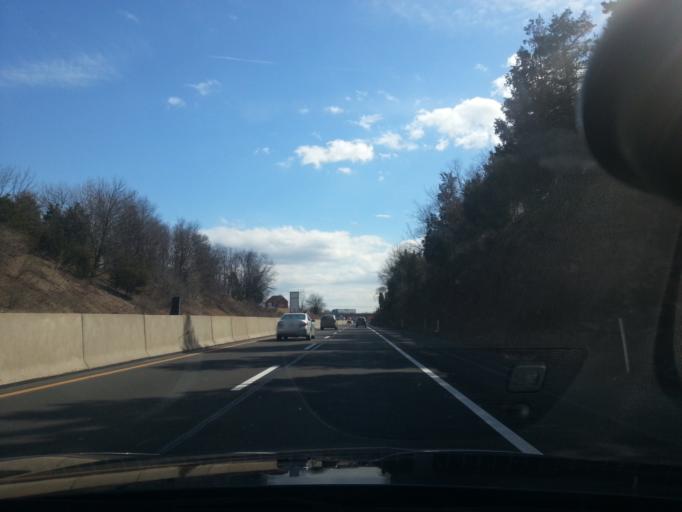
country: US
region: Pennsylvania
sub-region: Montgomery County
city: Harleysville
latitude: 40.3042
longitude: -75.3714
